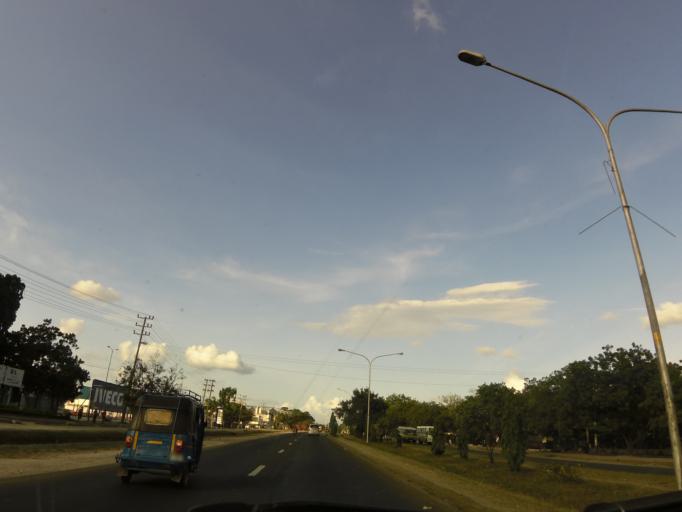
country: TZ
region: Dar es Salaam
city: Dar es Salaam
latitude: -6.8477
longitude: 39.2376
